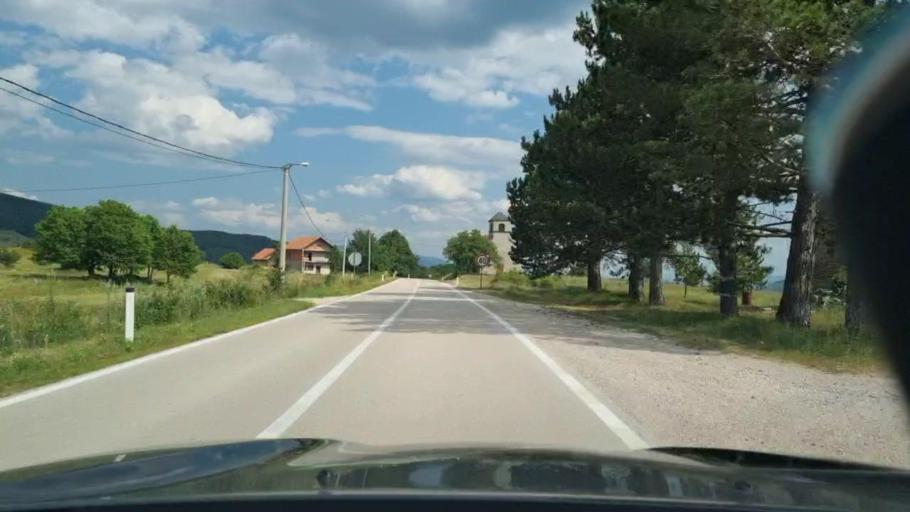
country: BA
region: Federation of Bosnia and Herzegovina
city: Bosansko Grahovo
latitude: 44.1198
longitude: 16.5347
